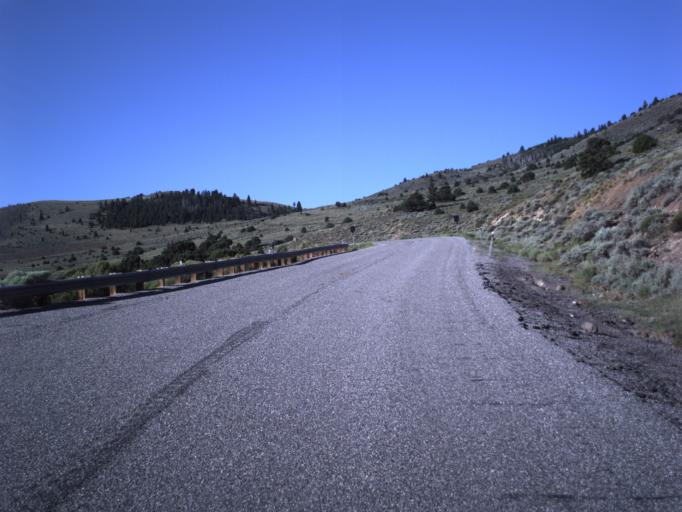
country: US
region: Utah
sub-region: Wayne County
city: Loa
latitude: 38.6084
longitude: -111.4613
